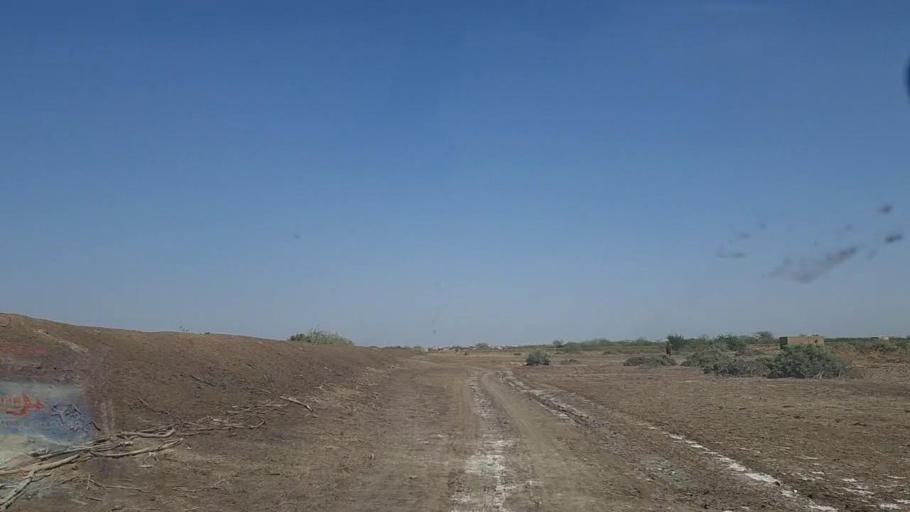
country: PK
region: Sindh
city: Chuhar Jamali
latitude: 24.2724
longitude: 67.7550
